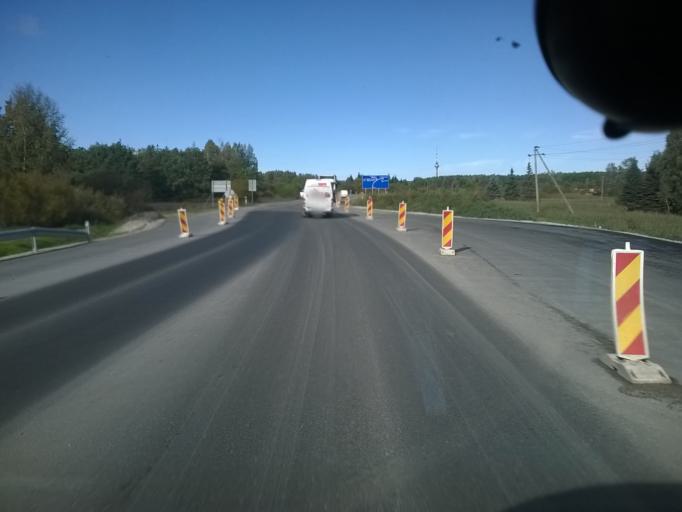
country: EE
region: Harju
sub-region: Joelaehtme vald
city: Loo
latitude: 59.4391
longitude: 24.9122
